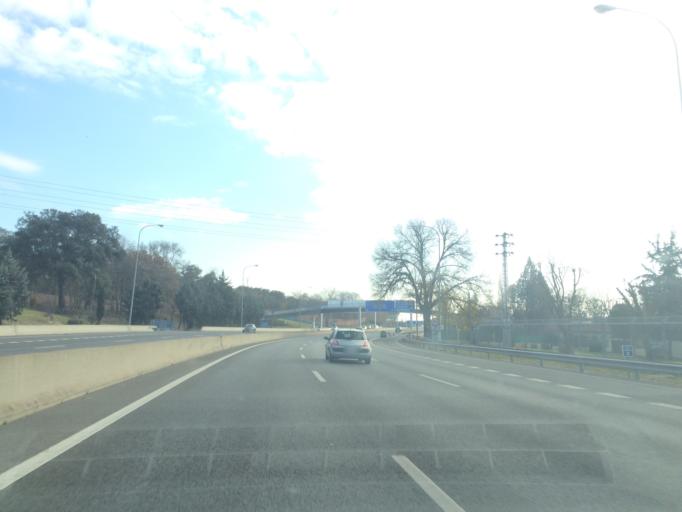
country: ES
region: Madrid
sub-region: Provincia de Madrid
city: Moncloa-Aravaca
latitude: 40.4613
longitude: -3.7463
